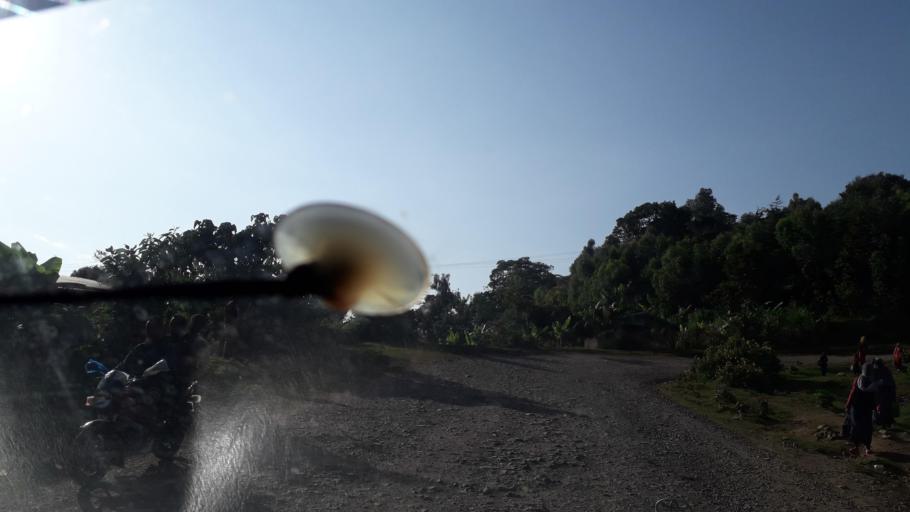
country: ET
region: Oromiya
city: Jima
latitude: 7.4857
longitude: 36.8794
